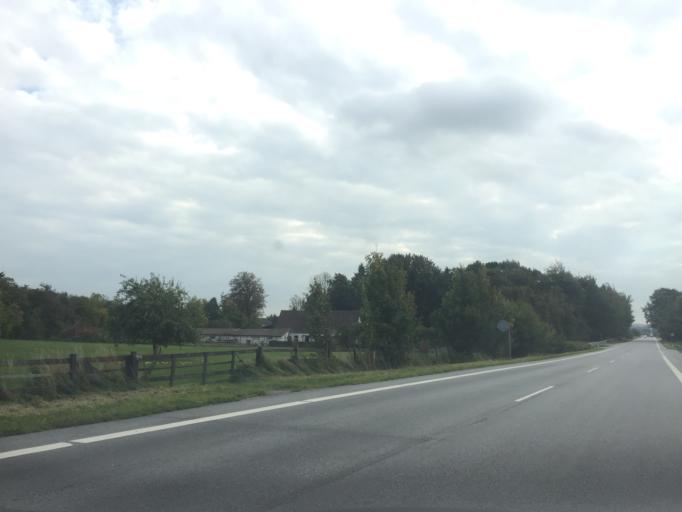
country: DK
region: Zealand
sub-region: Faxe Kommune
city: Ronnede
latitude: 55.1833
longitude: 11.9850
